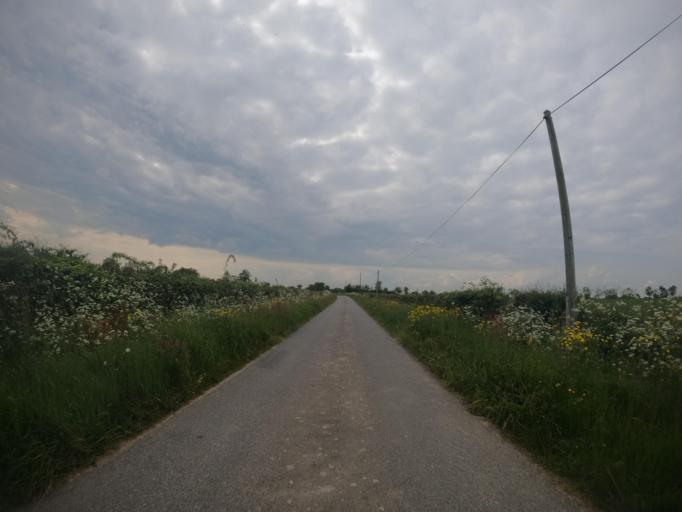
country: FR
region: Poitou-Charentes
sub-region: Departement des Deux-Sevres
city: Chiche
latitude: 46.8552
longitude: -0.3214
